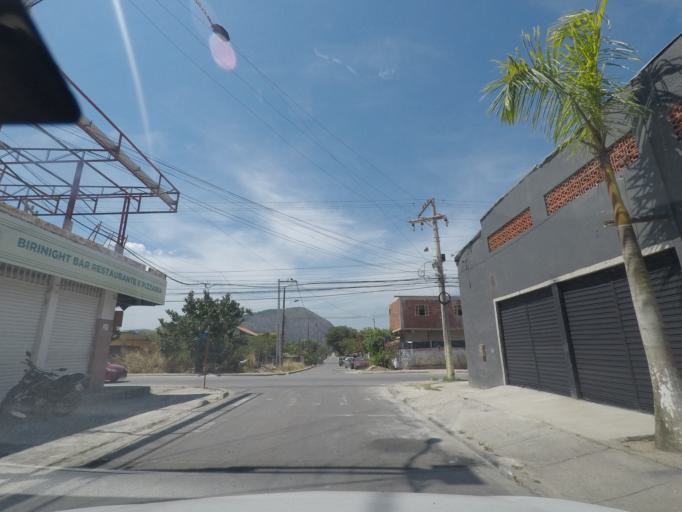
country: BR
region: Rio de Janeiro
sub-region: Marica
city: Marica
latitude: -22.9649
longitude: -42.9585
